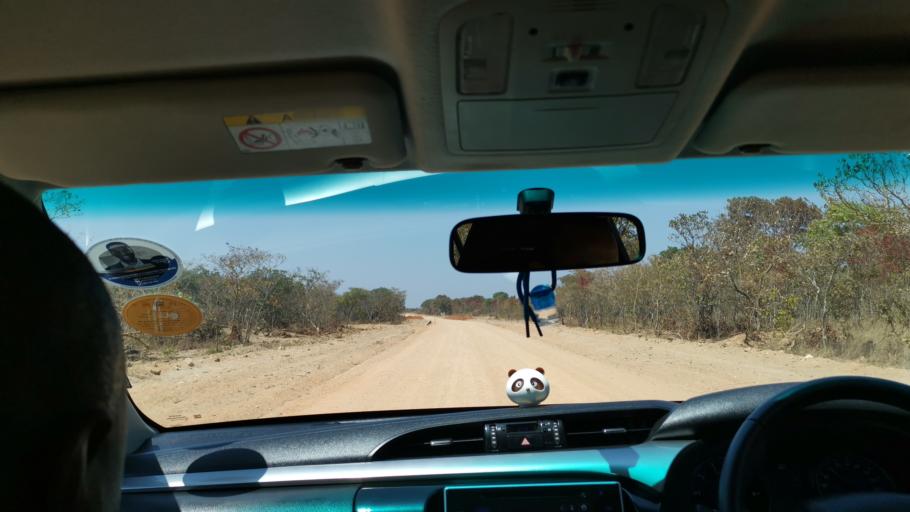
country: ZM
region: Central
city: Mkushi
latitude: -13.6491
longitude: 29.7522
